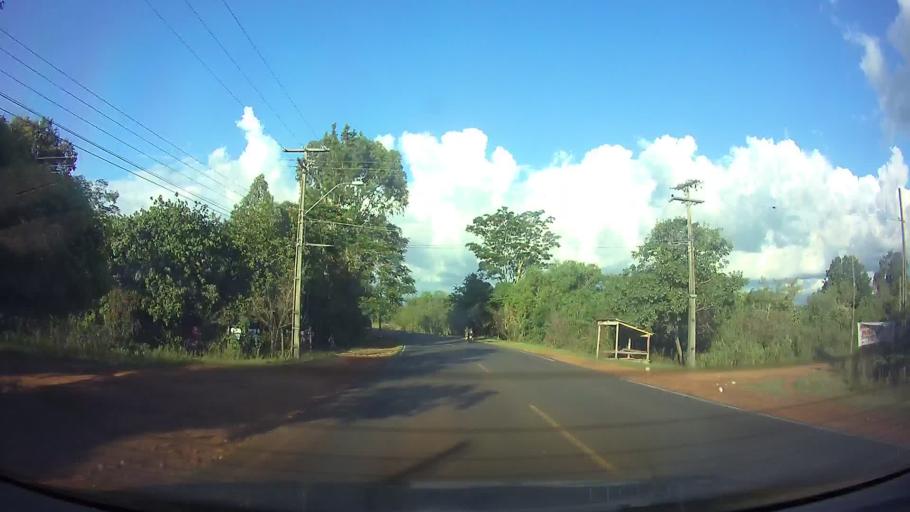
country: PY
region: Cordillera
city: Emboscada
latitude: -25.1657
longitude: -57.2703
